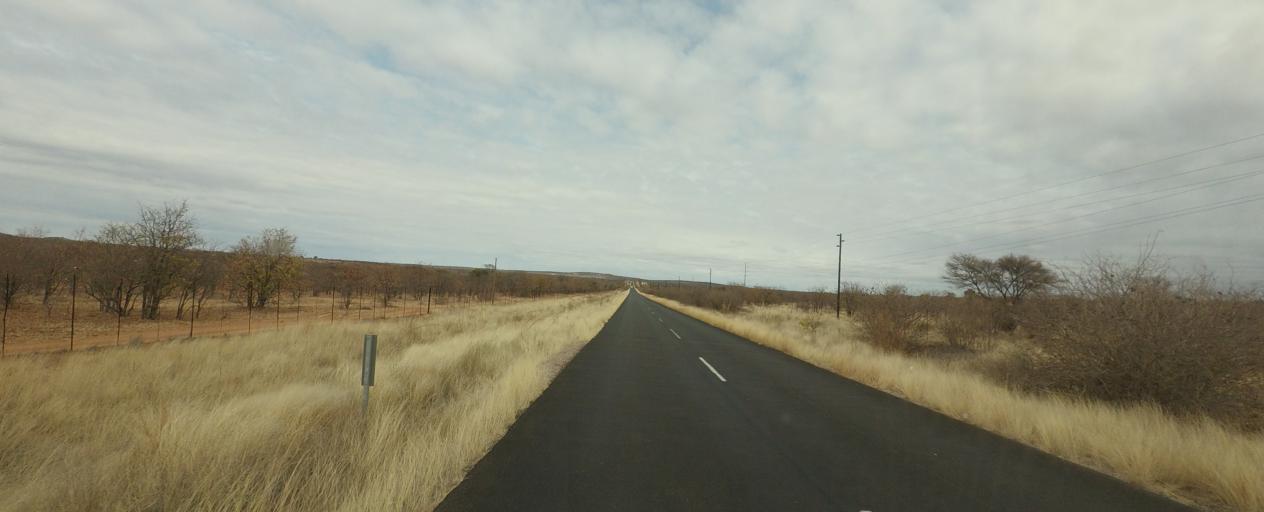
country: ZW
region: Matabeleland South
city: Beitbridge
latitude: -22.4304
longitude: 29.4439
